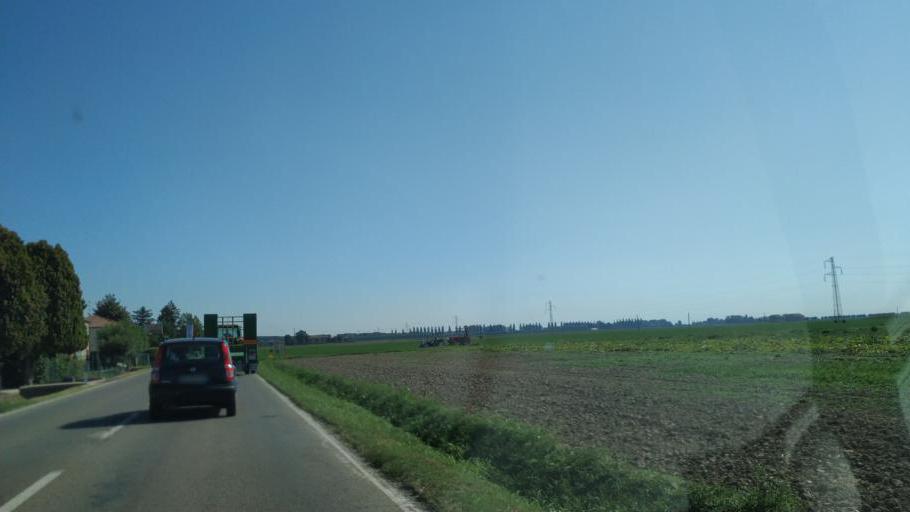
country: IT
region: Emilia-Romagna
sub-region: Provincia di Ferrara
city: San Carlo
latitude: 44.8054
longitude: 11.4232
